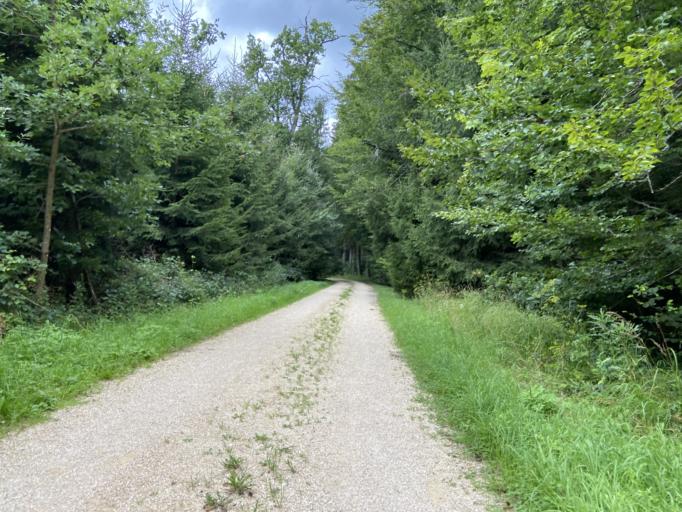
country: DE
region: Baden-Wuerttemberg
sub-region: Tuebingen Region
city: Sigmaringendorf
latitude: 48.0863
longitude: 9.2684
